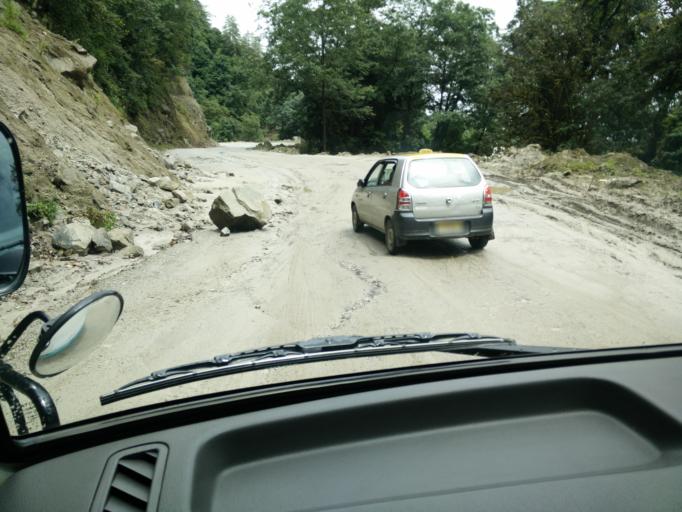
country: BT
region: Thimphu
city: Lungtenzampa
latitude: 27.5159
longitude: 89.7493
